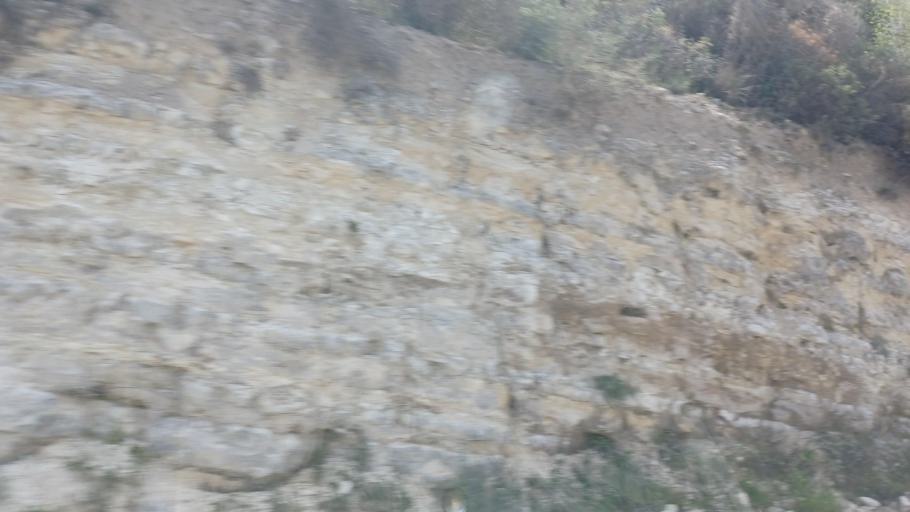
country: CY
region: Limassol
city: Pachna
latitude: 34.7697
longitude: 32.7507
